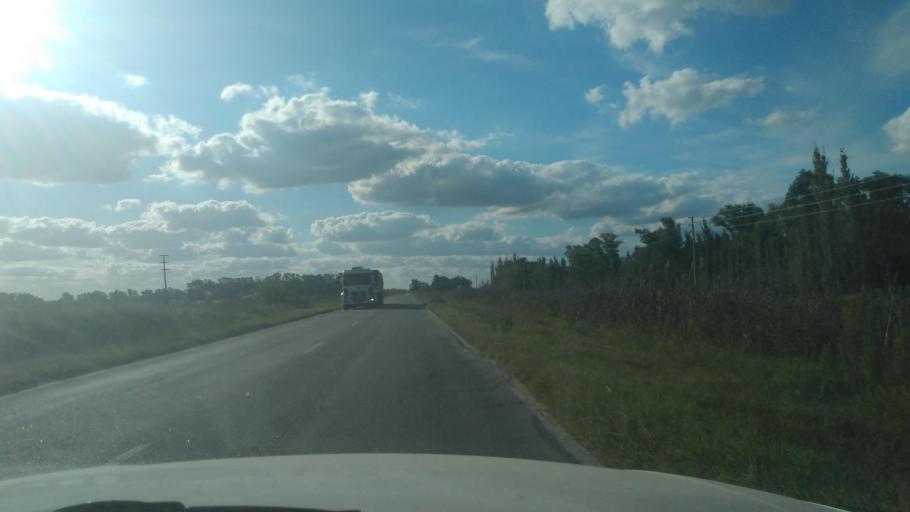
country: AR
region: Buenos Aires
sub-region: Partido de Mercedes
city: Mercedes
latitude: -34.7504
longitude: -59.3808
